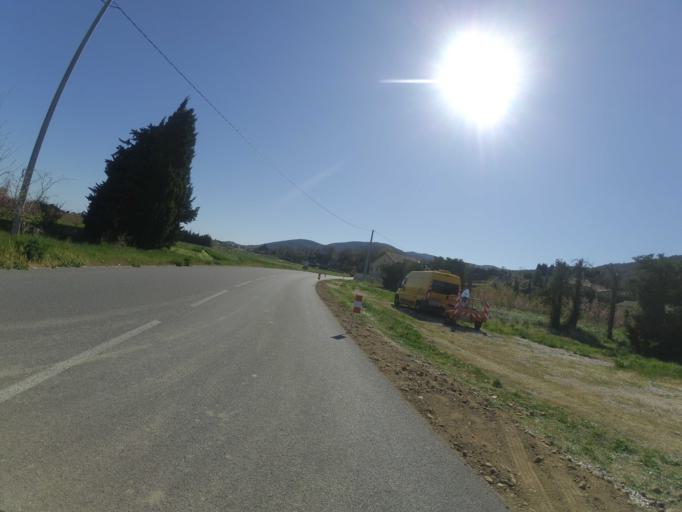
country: FR
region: Languedoc-Roussillon
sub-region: Departement des Pyrenees-Orientales
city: Ille-sur-Tet
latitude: 42.6563
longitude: 2.6155
